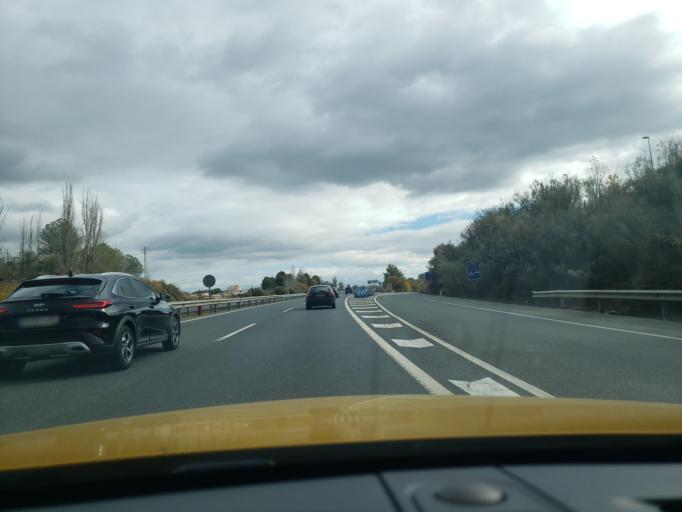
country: ES
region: Andalusia
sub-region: Provincia de Granada
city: Lachar
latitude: 37.1934
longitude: -3.8411
